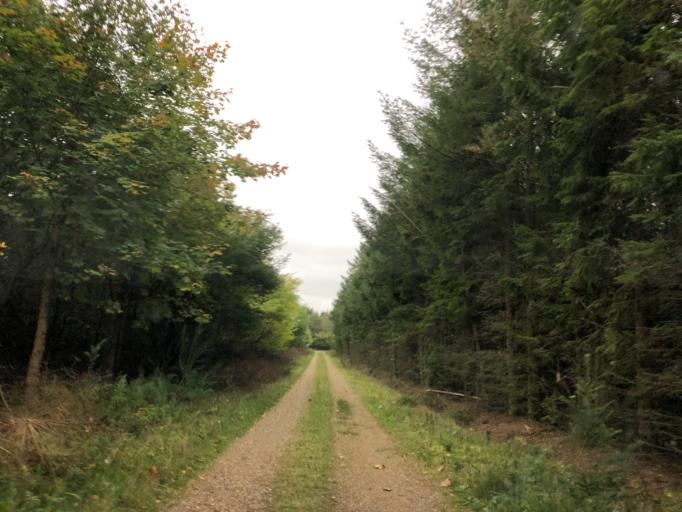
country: DK
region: Central Jutland
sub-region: Holstebro Kommune
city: Ulfborg
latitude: 56.2207
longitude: 8.4514
